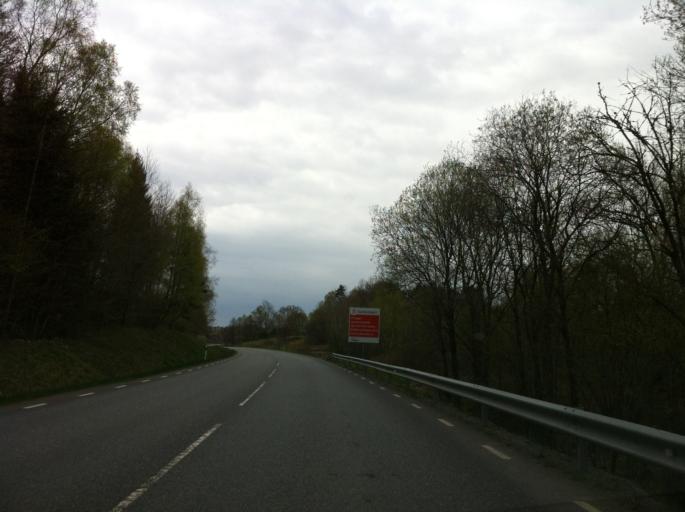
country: SE
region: Halland
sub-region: Falkenbergs Kommun
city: Falkenberg
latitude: 57.0925
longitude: 12.6751
